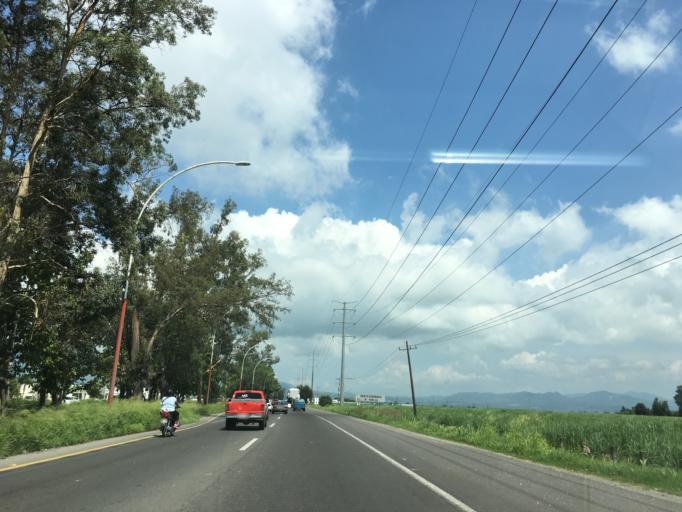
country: MX
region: Nayarit
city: Xalisco
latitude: 21.4673
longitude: -104.8832
